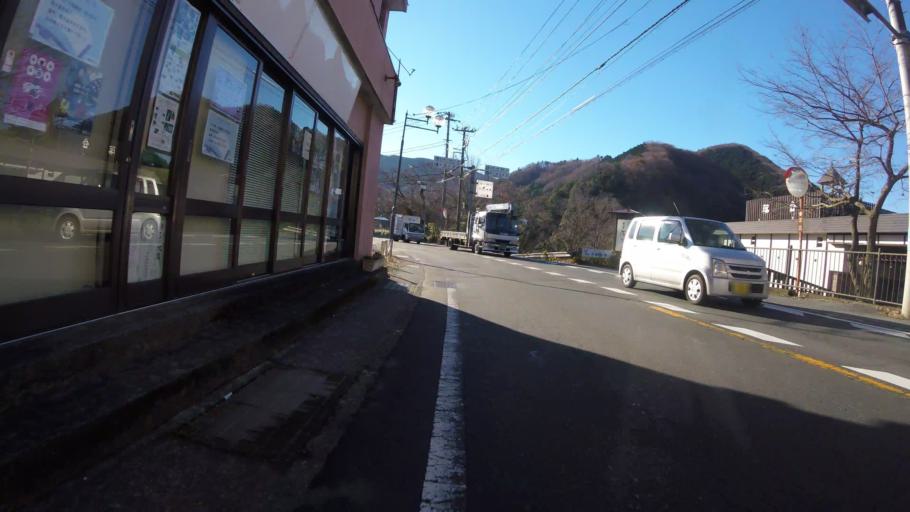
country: JP
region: Shizuoka
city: Heda
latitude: 34.8897
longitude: 138.9289
